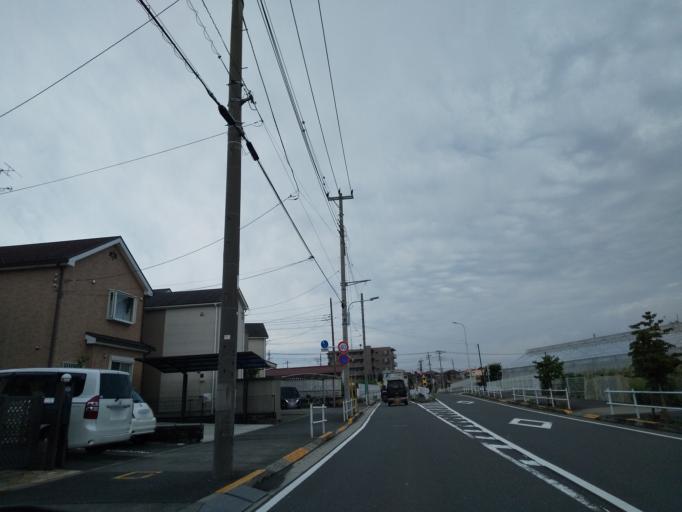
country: JP
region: Tokyo
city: Hino
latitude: 35.6812
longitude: 139.3787
